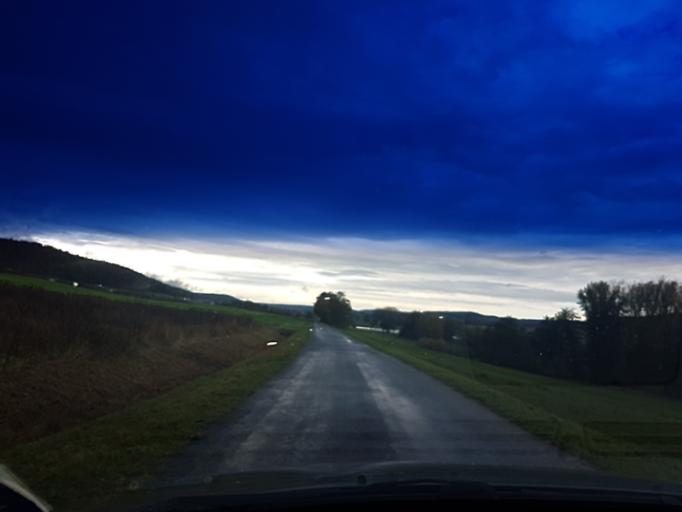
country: DE
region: Bavaria
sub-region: Regierungsbezirk Mittelfranken
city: Burghaslach
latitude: 49.7627
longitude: 10.5610
